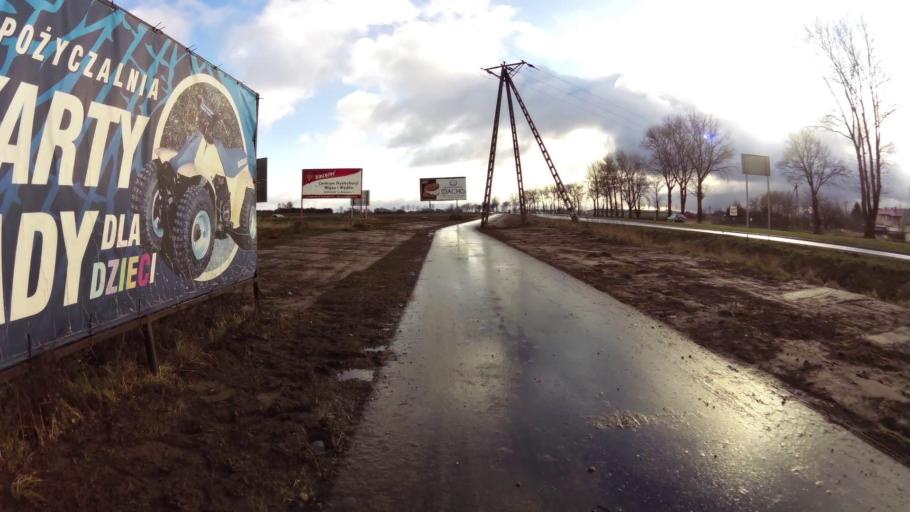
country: PL
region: West Pomeranian Voivodeship
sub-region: Koszalin
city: Koszalin
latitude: 54.1620
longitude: 16.2234
